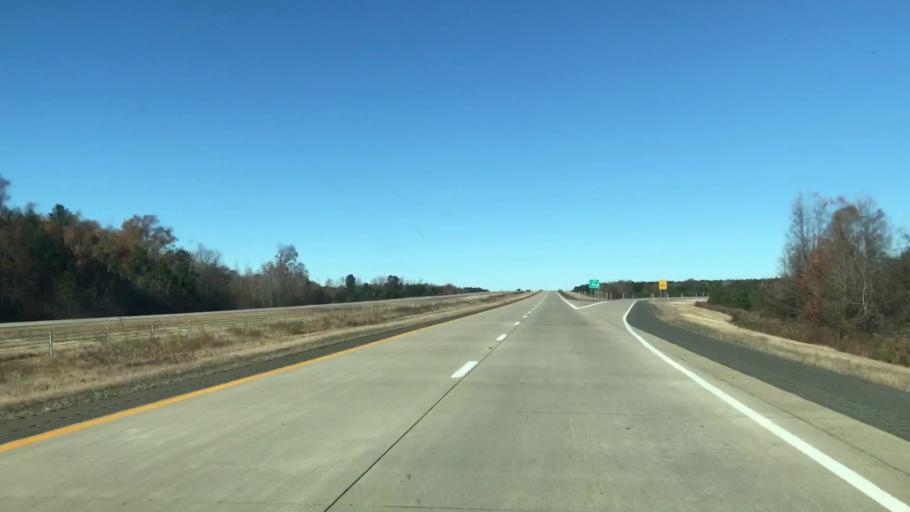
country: US
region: Texas
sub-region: Bowie County
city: Texarkana
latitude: 33.2467
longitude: -93.8798
